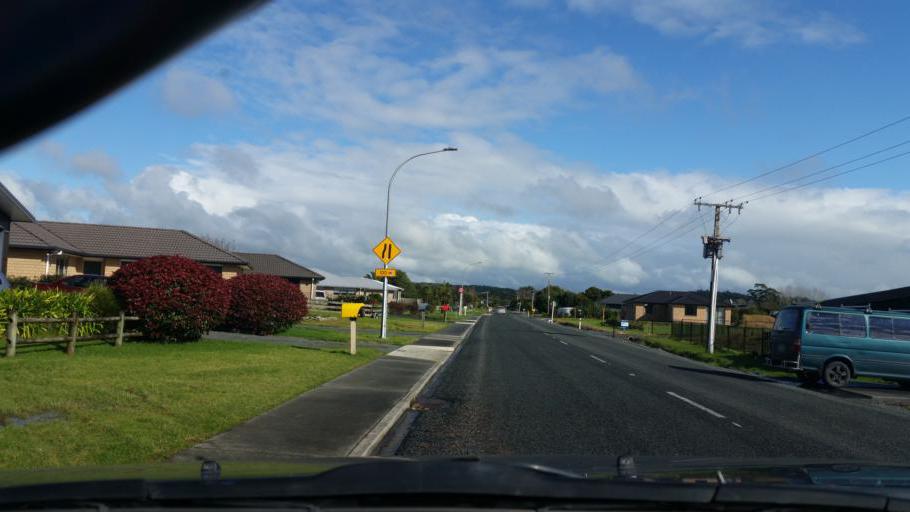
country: NZ
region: Auckland
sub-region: Auckland
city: Wellsford
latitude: -36.0875
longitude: 174.5756
